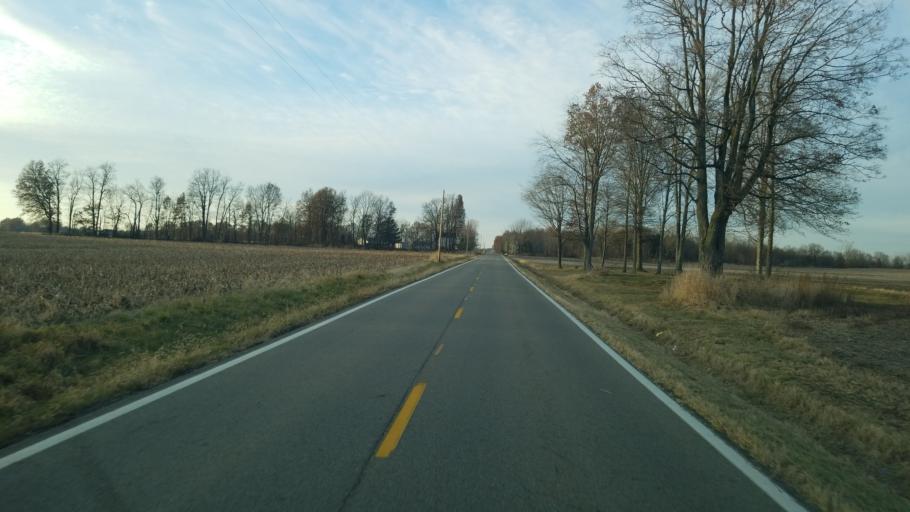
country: US
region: Ohio
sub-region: Knox County
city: Centerburg
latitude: 40.2540
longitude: -82.5928
